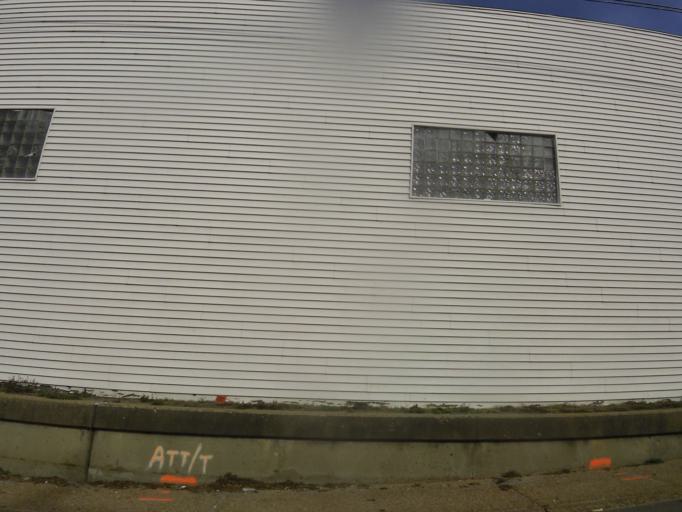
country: US
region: Virginia
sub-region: City of Hopewell
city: Hopewell
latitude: 37.3026
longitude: -77.2836
